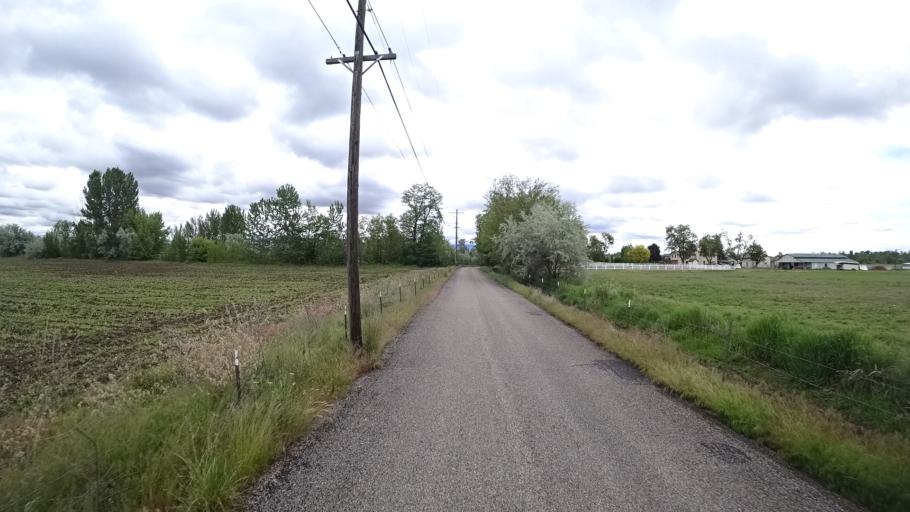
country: US
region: Idaho
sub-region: Ada County
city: Eagle
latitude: 43.6847
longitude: -116.3778
